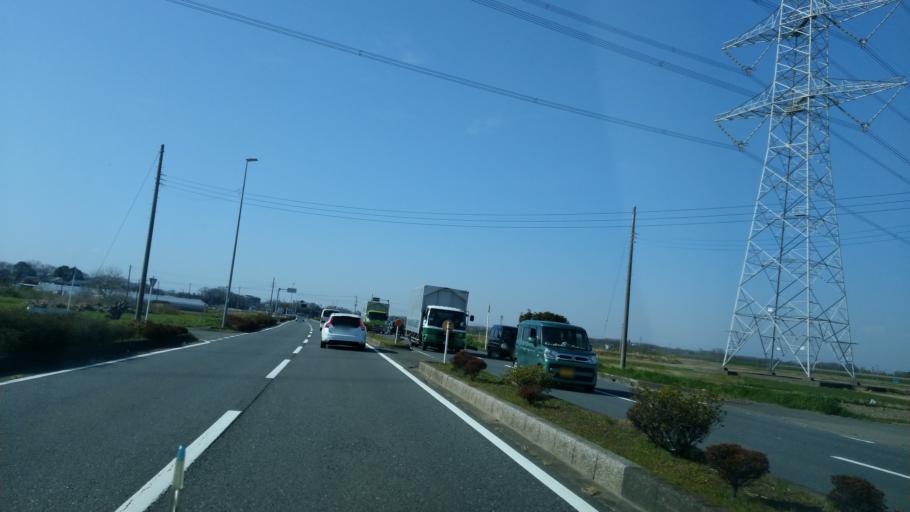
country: JP
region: Saitama
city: Sakado
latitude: 36.0036
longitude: 139.4483
